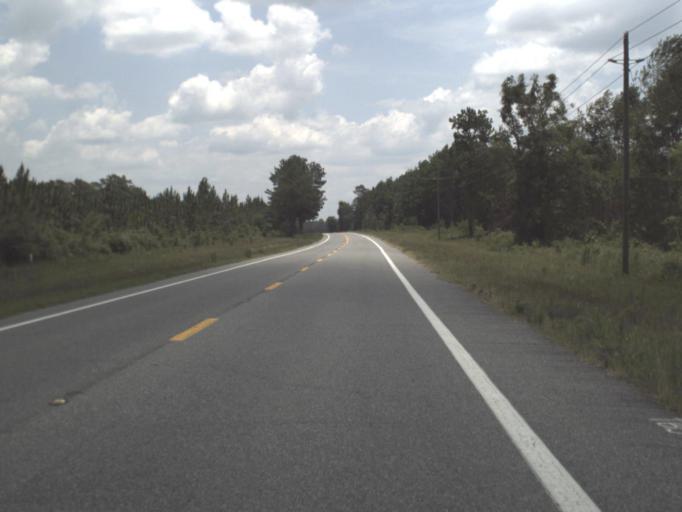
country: US
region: Florida
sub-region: Madison County
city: Madison
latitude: 30.4866
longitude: -83.1878
